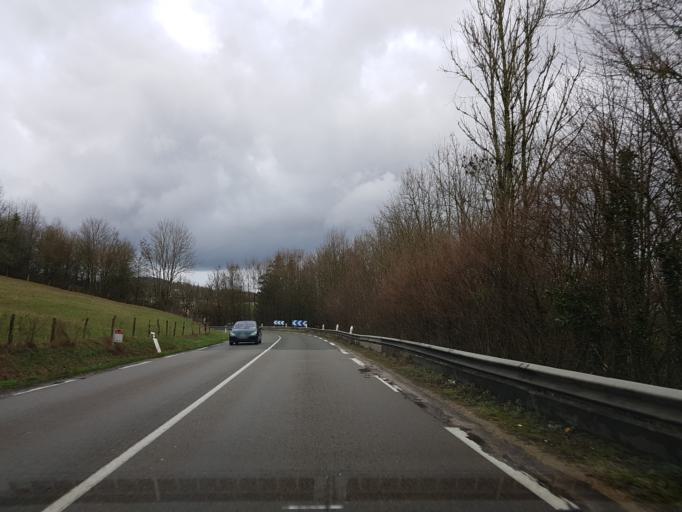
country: FR
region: Franche-Comte
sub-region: Departement de la Haute-Saone
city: Magny-Vernois
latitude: 47.6654
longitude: 6.3784
